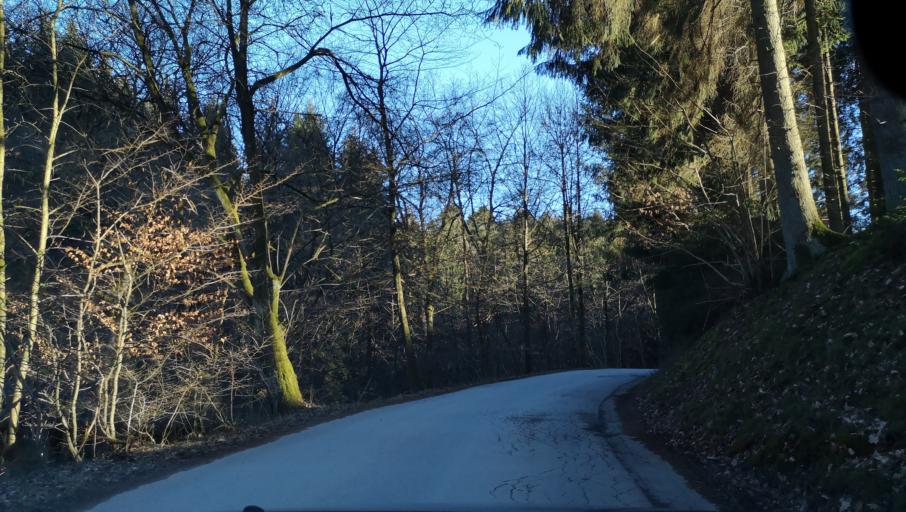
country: DE
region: North Rhine-Westphalia
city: Ennepetal
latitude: 51.2597
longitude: 7.3706
